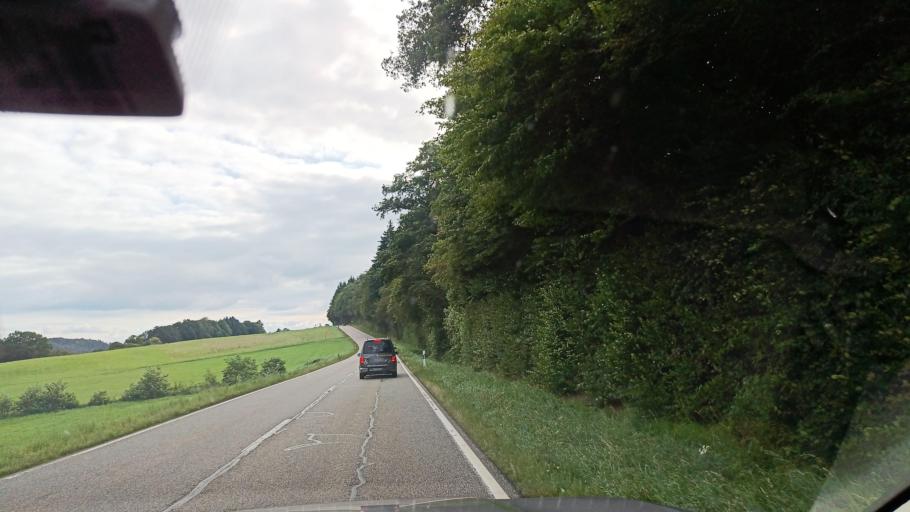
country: DE
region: Saarland
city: Wadern
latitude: 49.5539
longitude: 6.9121
